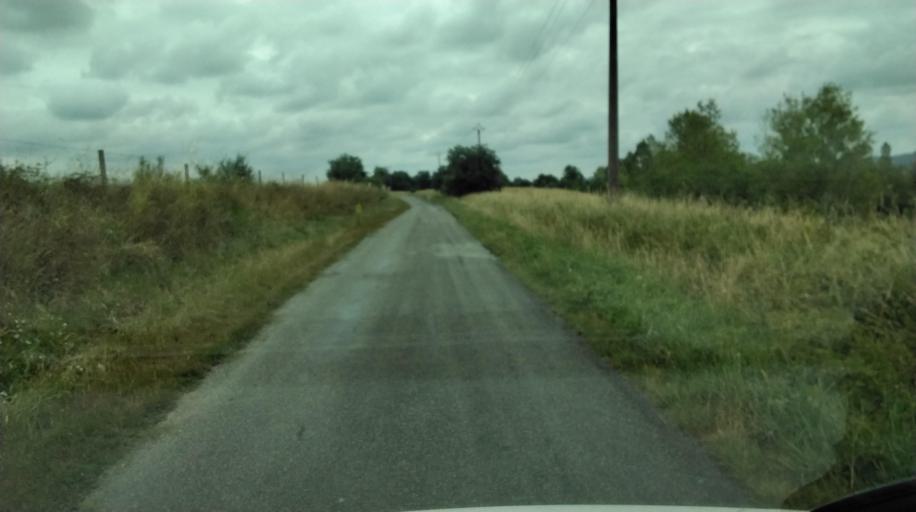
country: FR
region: Midi-Pyrenees
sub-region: Departement de la Haute-Garonne
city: Martres-Tolosane
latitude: 43.2101
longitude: 1.0464
